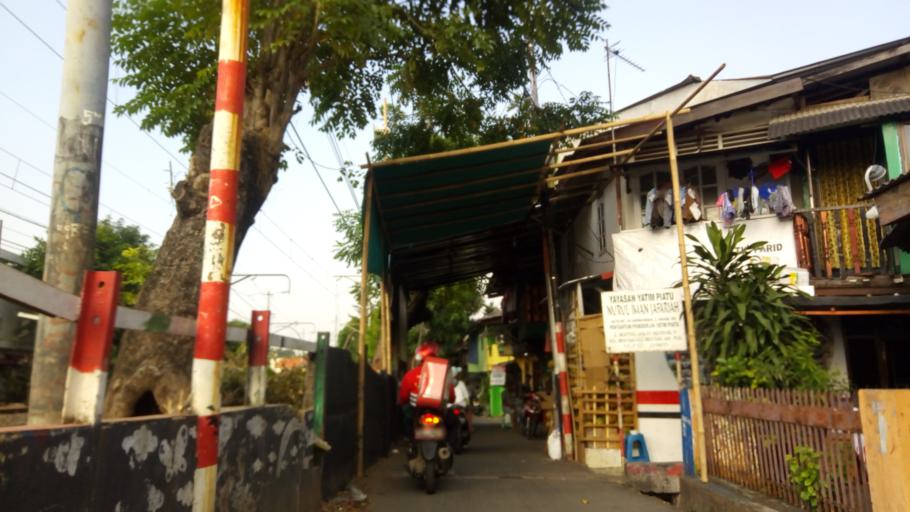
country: ID
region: Jakarta Raya
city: Jakarta
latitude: -6.2067
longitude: 106.8419
